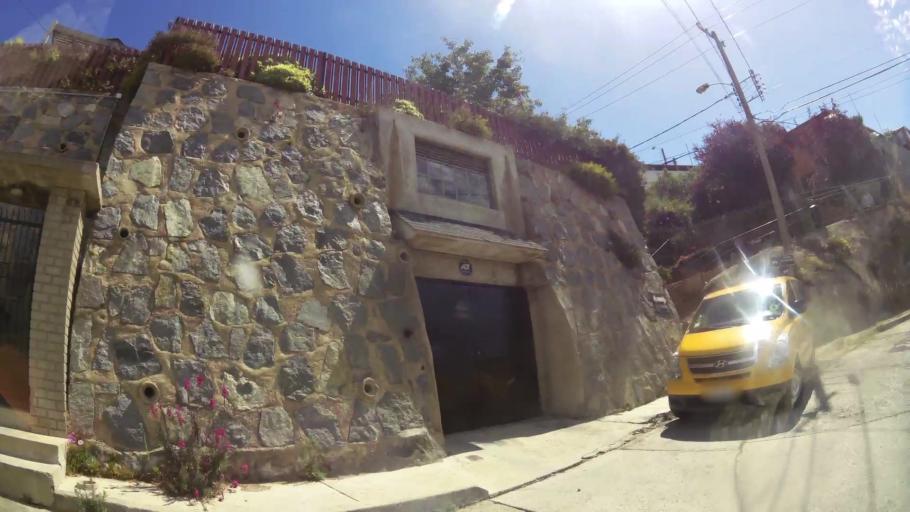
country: CL
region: Valparaiso
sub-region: Provincia de Valparaiso
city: Vina del Mar
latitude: -33.0371
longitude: -71.5769
